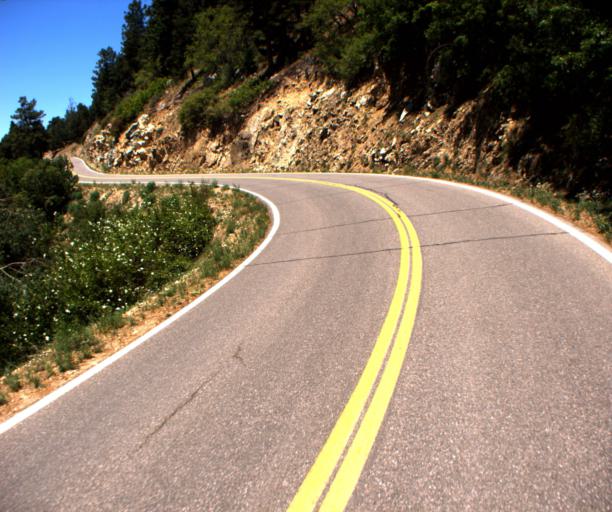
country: US
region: Arizona
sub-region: Graham County
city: Swift Trail Junction
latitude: 32.6486
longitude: -109.8586
